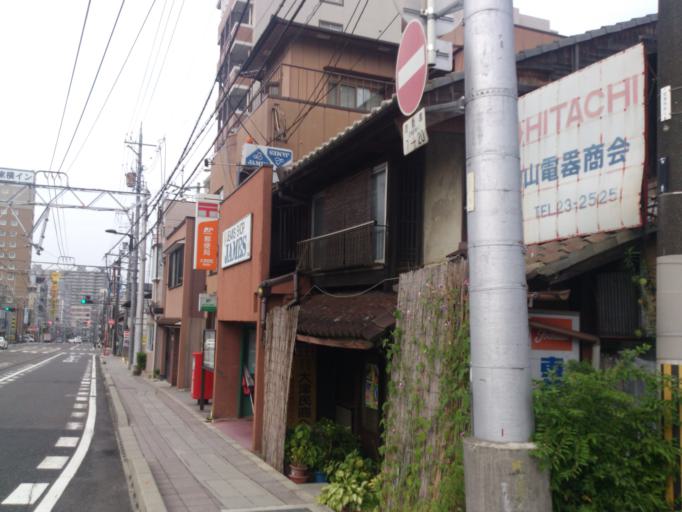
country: JP
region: Shiga Prefecture
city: Otsu-shi
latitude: 35.0063
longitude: 135.8616
